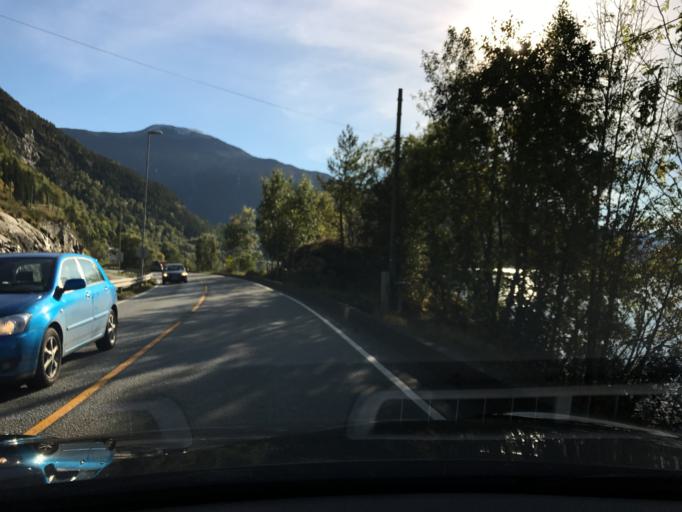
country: NO
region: Sogn og Fjordane
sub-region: Sogndal
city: Sogndalsfjora
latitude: 61.2275
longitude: 7.1251
